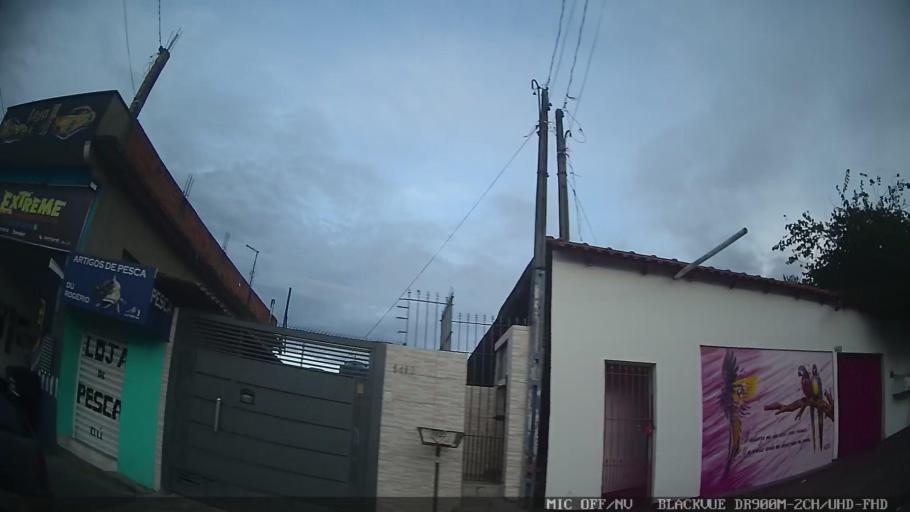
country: BR
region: Sao Paulo
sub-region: Itaquaquecetuba
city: Itaquaquecetuba
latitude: -23.4980
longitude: -46.3162
